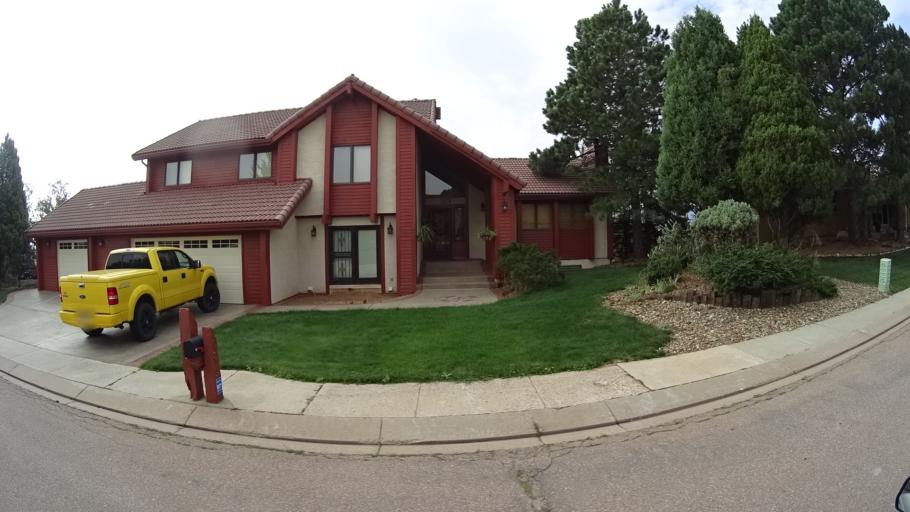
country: US
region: Colorado
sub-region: El Paso County
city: Air Force Academy
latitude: 38.9362
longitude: -104.8544
